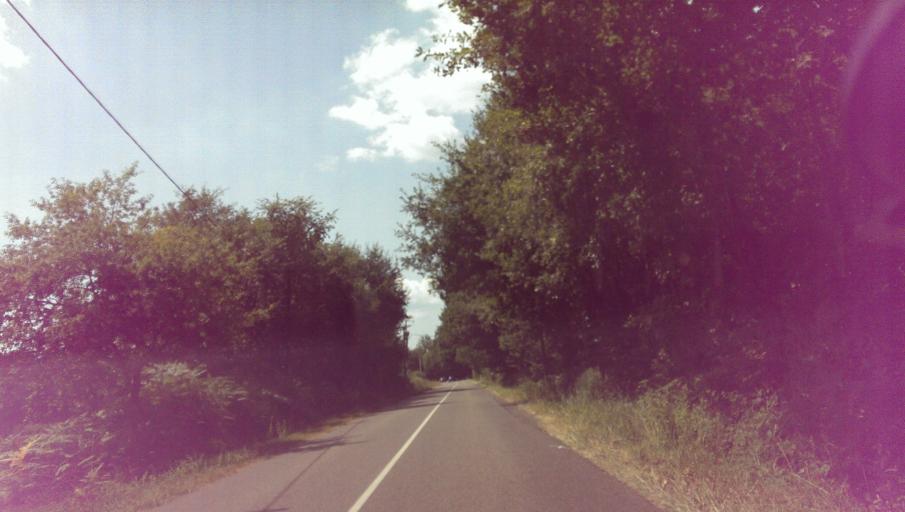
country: FR
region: Aquitaine
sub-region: Departement des Landes
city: Sabres
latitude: 44.1070
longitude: -0.5538
